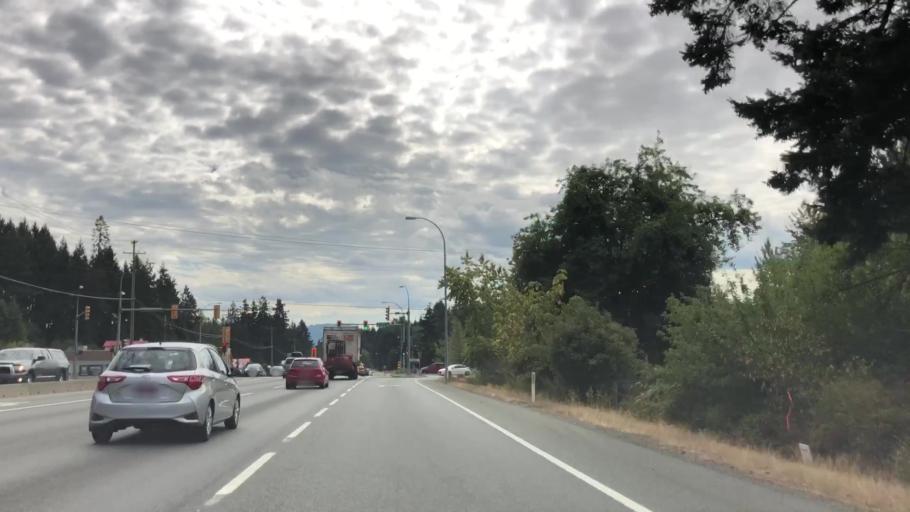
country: CA
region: British Columbia
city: Duncan
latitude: 48.8175
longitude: -123.7183
